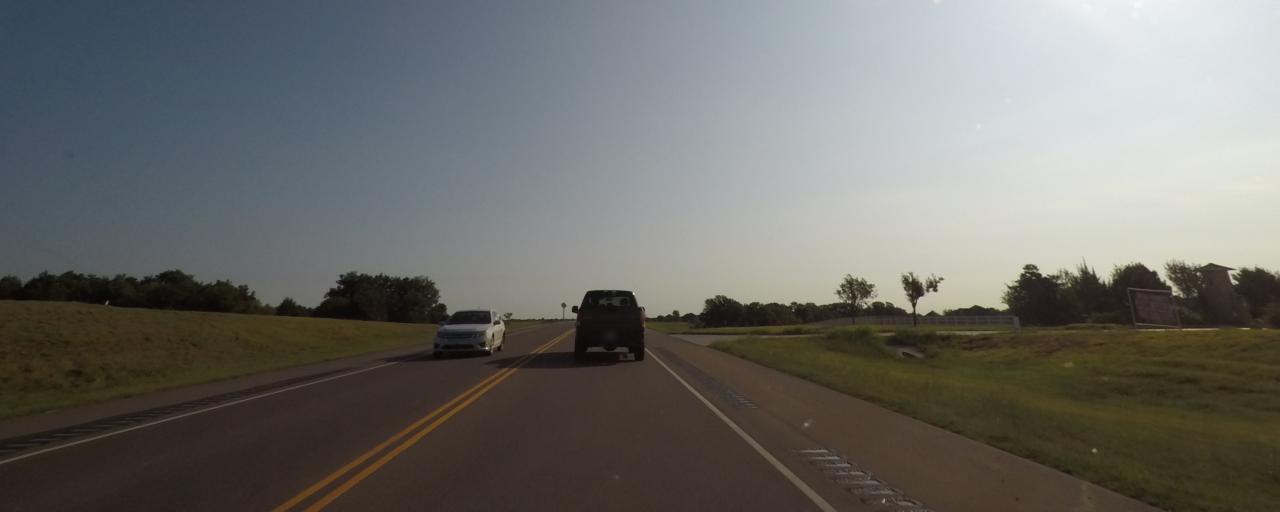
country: US
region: Oklahoma
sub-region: McClain County
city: Blanchard
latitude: 35.1132
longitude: -97.7134
